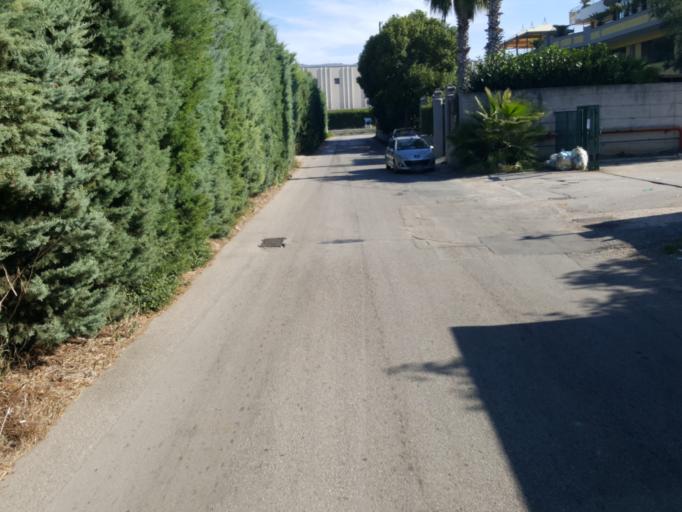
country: IT
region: Campania
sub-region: Provincia di Caserta
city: Pignataro Maggiore
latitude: 41.1633
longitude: 14.1640
